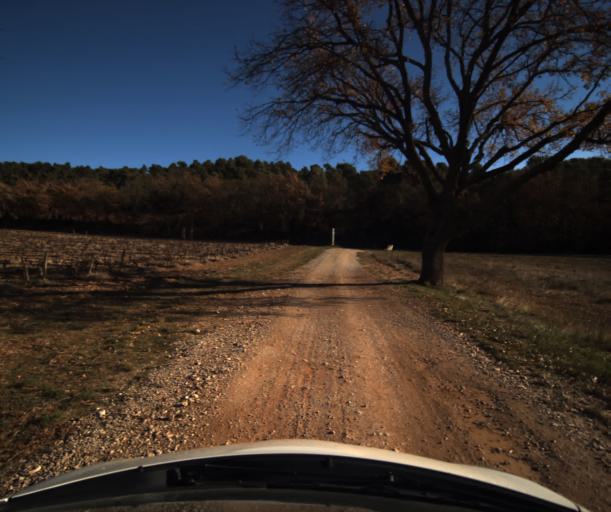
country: FR
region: Provence-Alpes-Cote d'Azur
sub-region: Departement du Vaucluse
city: Ansouis
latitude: 43.7078
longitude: 5.4689
